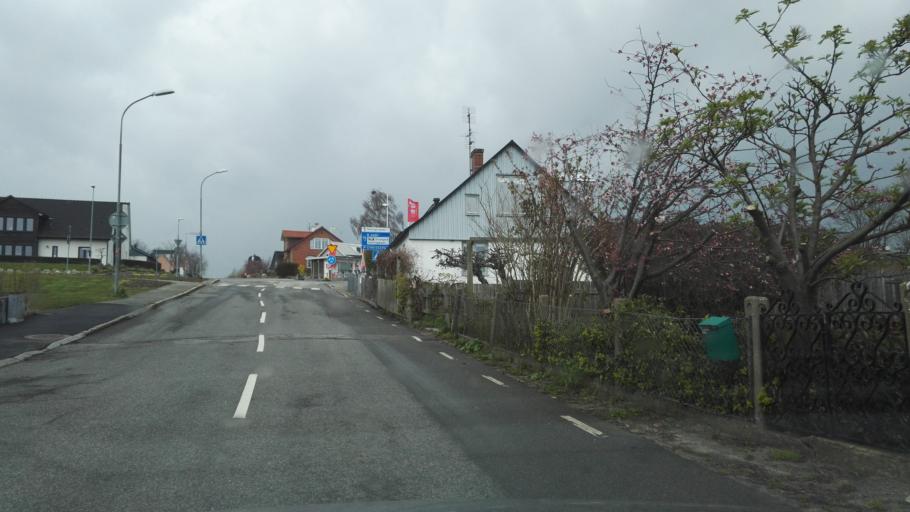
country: SE
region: Skane
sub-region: Simrishamns Kommun
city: Simrishamn
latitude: 55.4750
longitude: 14.2825
